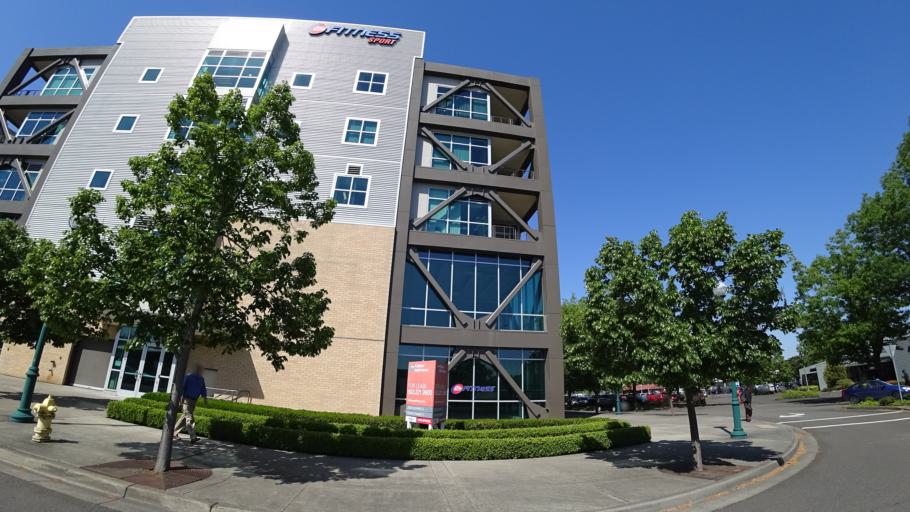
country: US
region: Oregon
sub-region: Washington County
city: Beaverton
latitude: 45.4894
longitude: -122.8067
